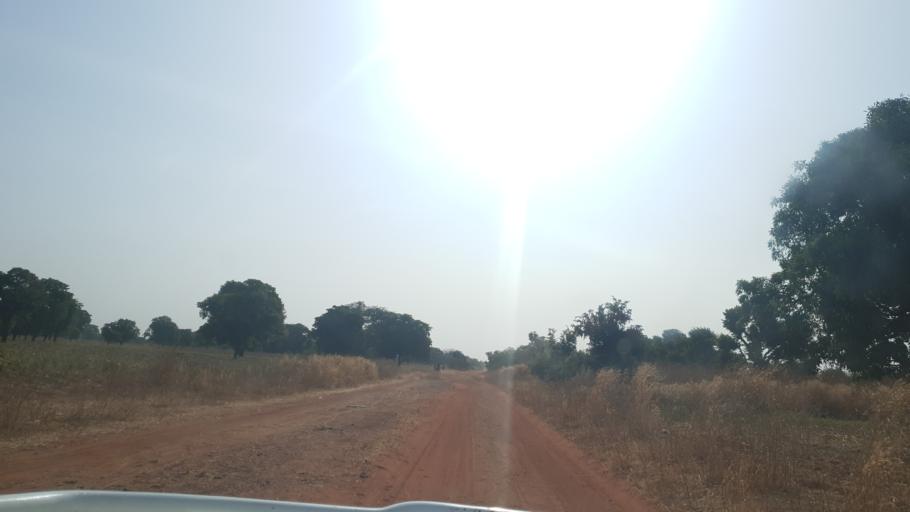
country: ML
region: Koulikoro
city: Dioila
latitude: 12.7053
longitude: -6.7695
